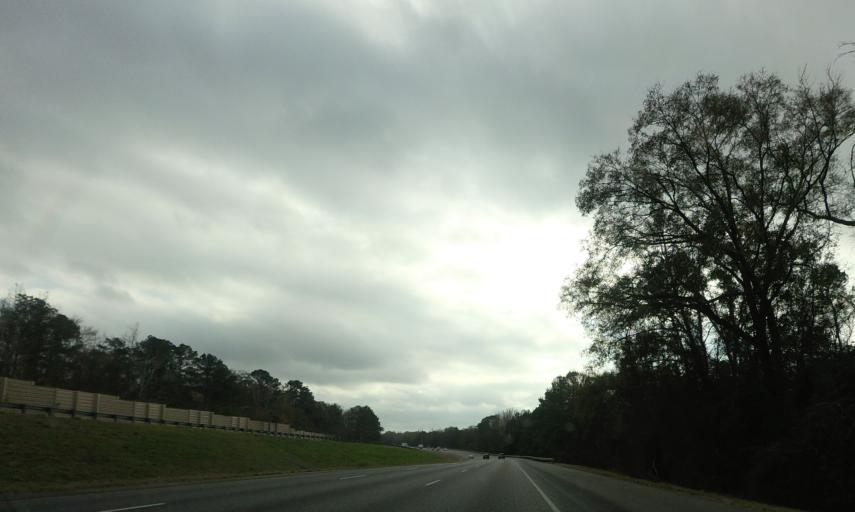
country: US
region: Georgia
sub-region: Bibb County
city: West Point
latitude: 32.7890
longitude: -83.7202
